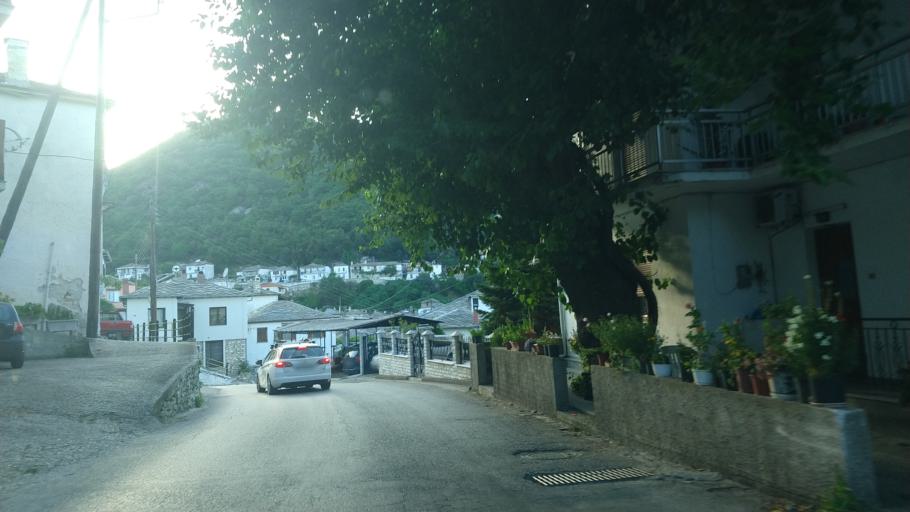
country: GR
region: East Macedonia and Thrace
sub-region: Nomos Kavalas
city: Potamia
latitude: 40.7302
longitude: 24.7303
